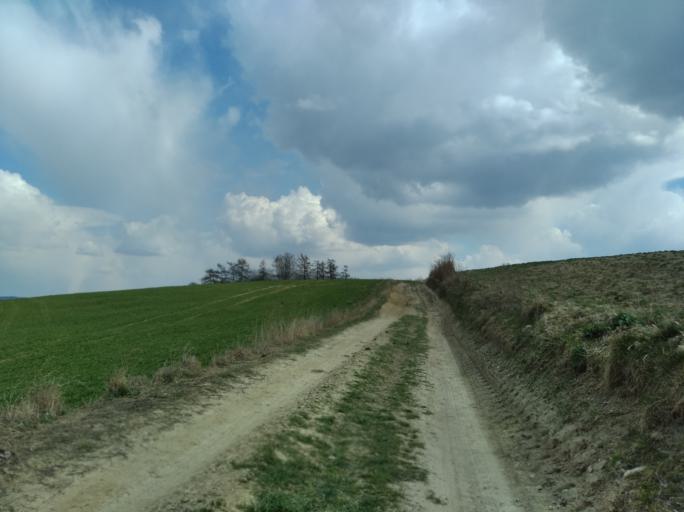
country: PL
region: Subcarpathian Voivodeship
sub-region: Powiat strzyzowski
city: Strzyzow
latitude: 49.9238
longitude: 21.7362
